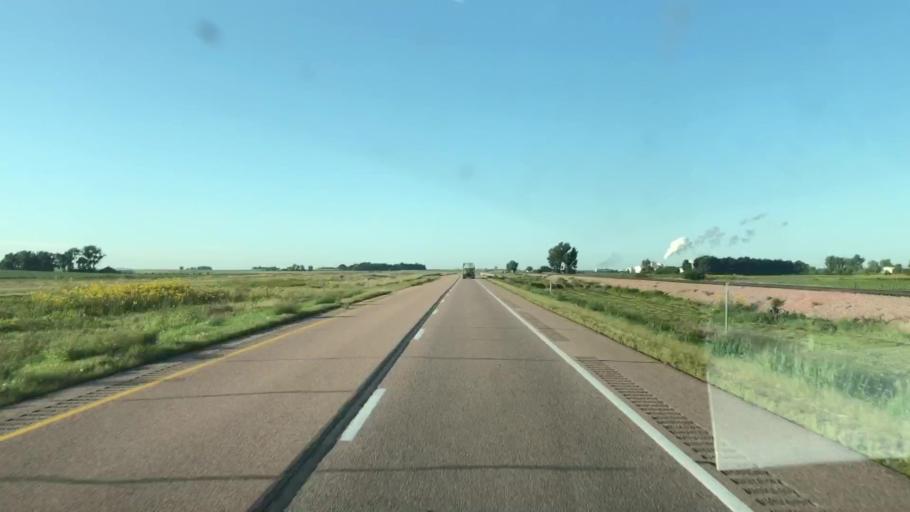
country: US
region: Iowa
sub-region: Osceola County
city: Sibley
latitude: 43.2933
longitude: -95.7959
